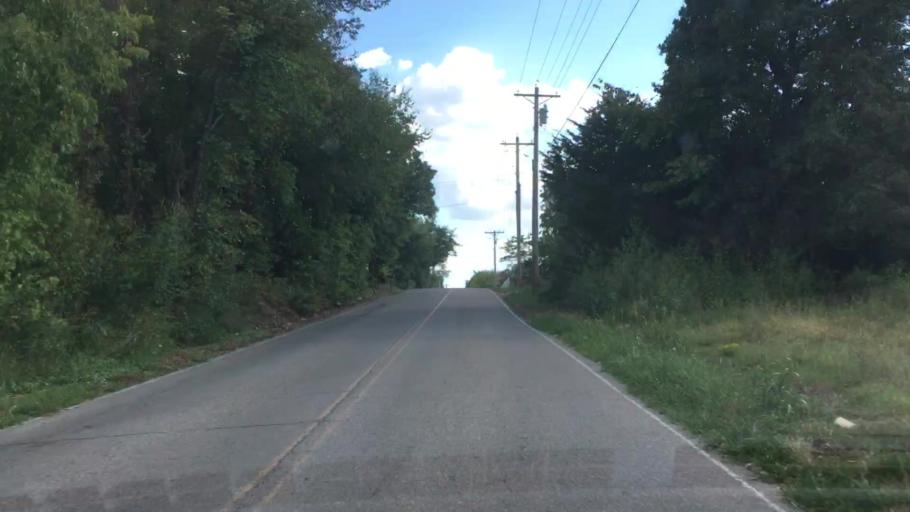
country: US
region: Oklahoma
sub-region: Cherokee County
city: Park Hill
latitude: 35.8070
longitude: -95.0739
